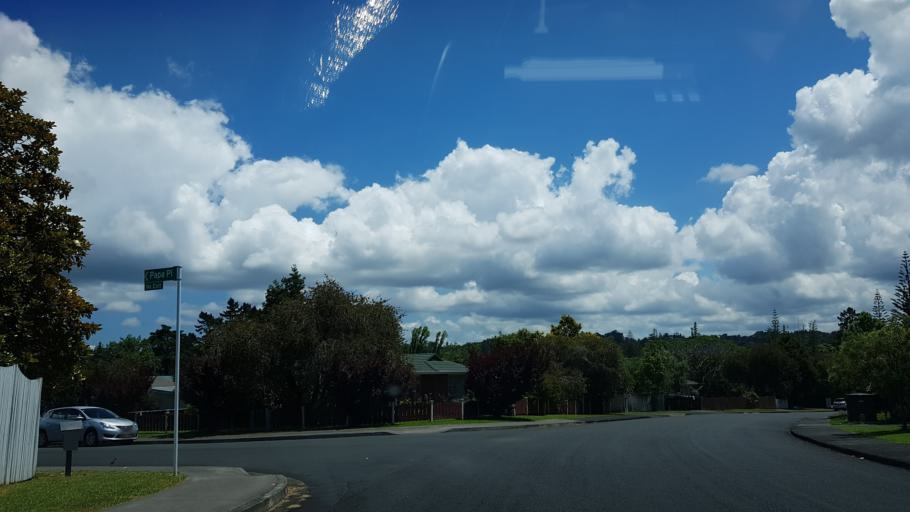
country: NZ
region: Auckland
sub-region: Auckland
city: North Shore
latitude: -36.7921
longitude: 174.6988
